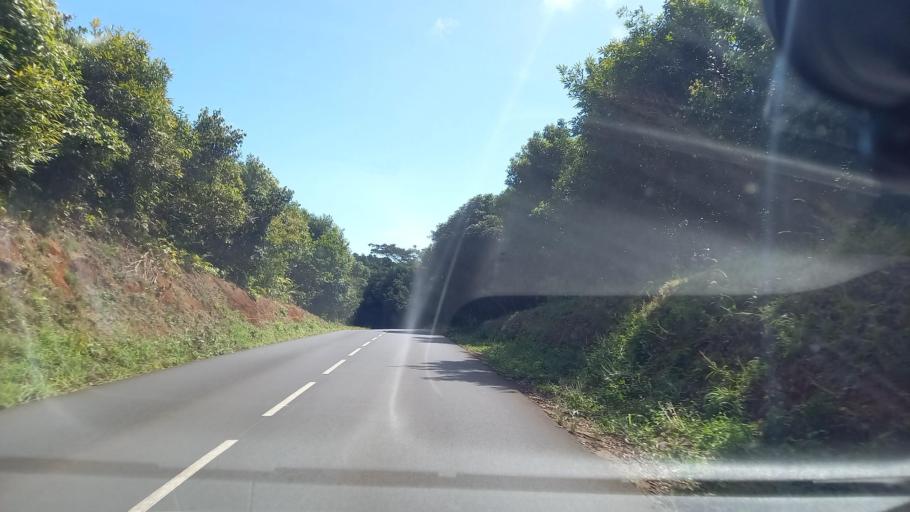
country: YT
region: Dembeni
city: Dembeni
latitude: -12.7895
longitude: 45.1619
